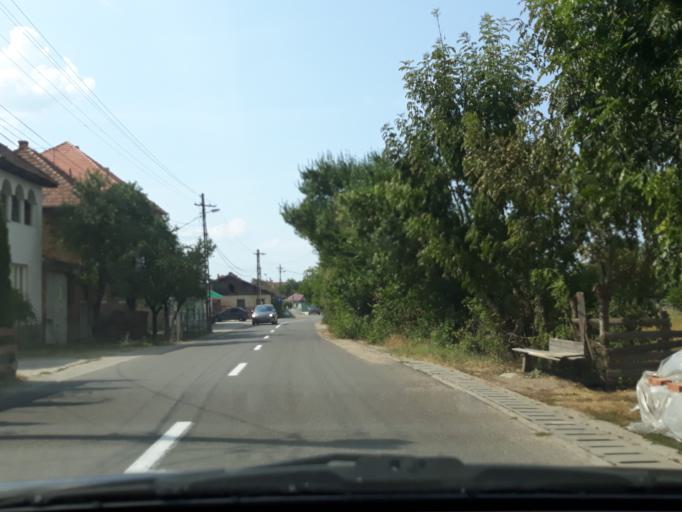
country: RO
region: Bihor
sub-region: Comuna Pietroasa
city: Pietroasa
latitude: 46.5905
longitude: 22.5599
